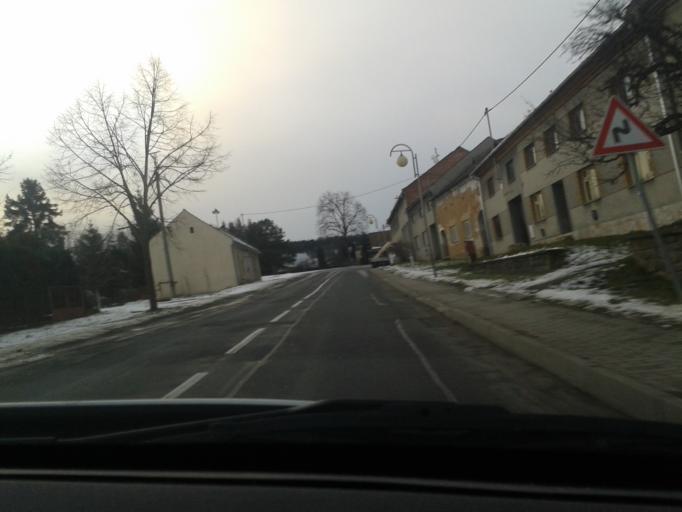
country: CZ
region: Olomoucky
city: Pteni
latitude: 49.4887
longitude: 16.9572
